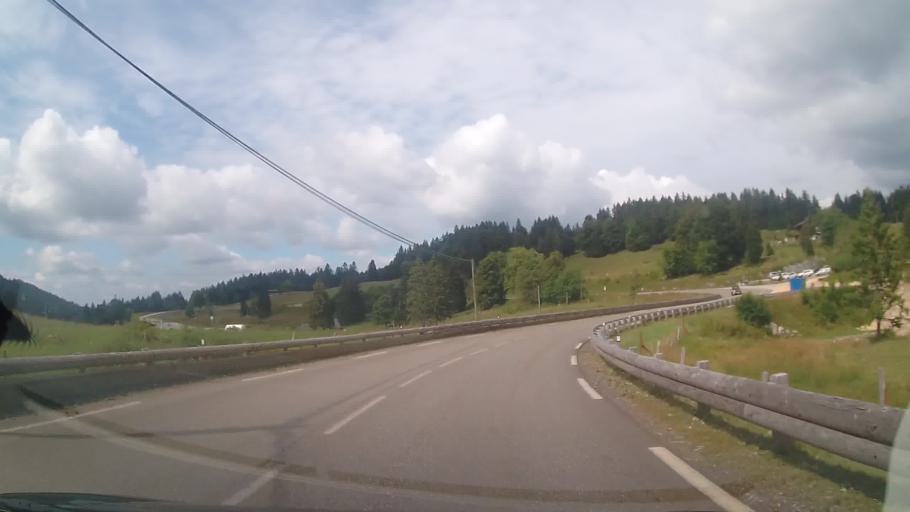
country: FR
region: Franche-Comte
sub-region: Departement du Jura
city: Les Rousses
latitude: 46.4458
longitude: 6.0808
